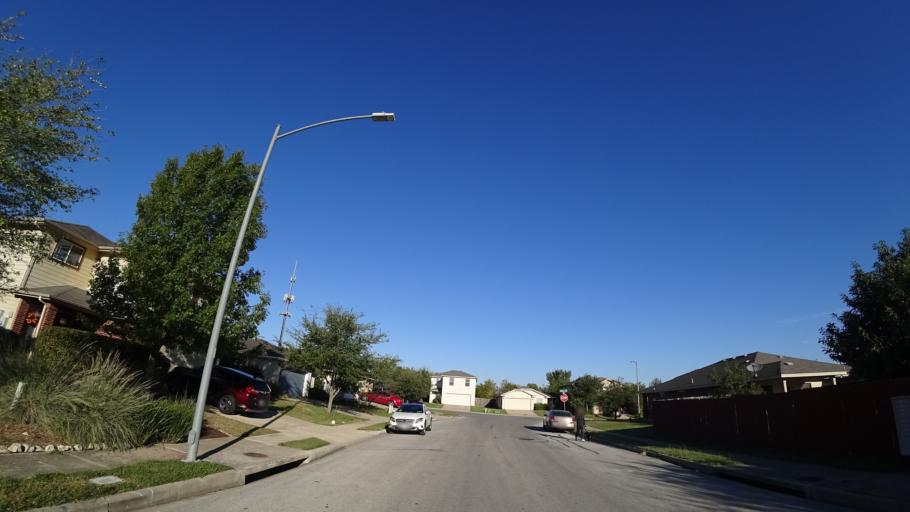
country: US
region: Texas
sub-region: Travis County
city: Austin
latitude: 30.2221
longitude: -97.6950
